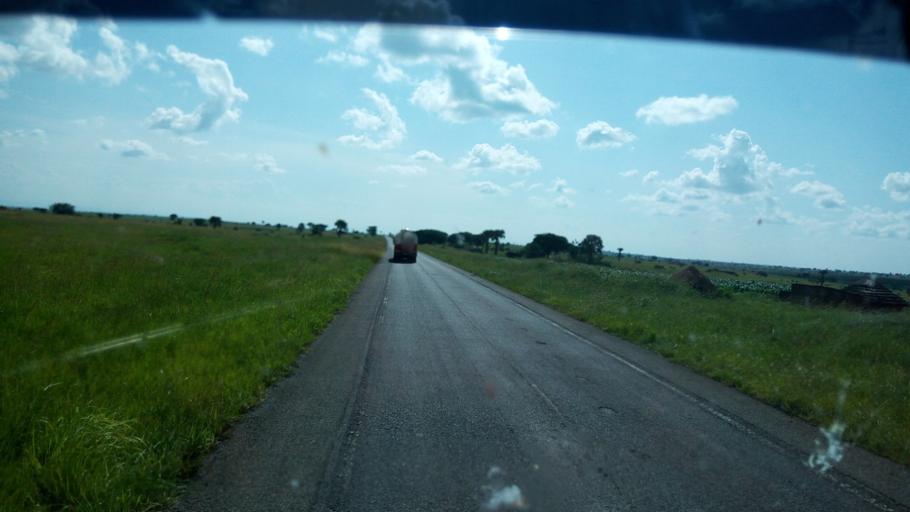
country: UG
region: Northern Region
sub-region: Nwoya District
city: Nwoya
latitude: 2.5596
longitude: 31.6936
